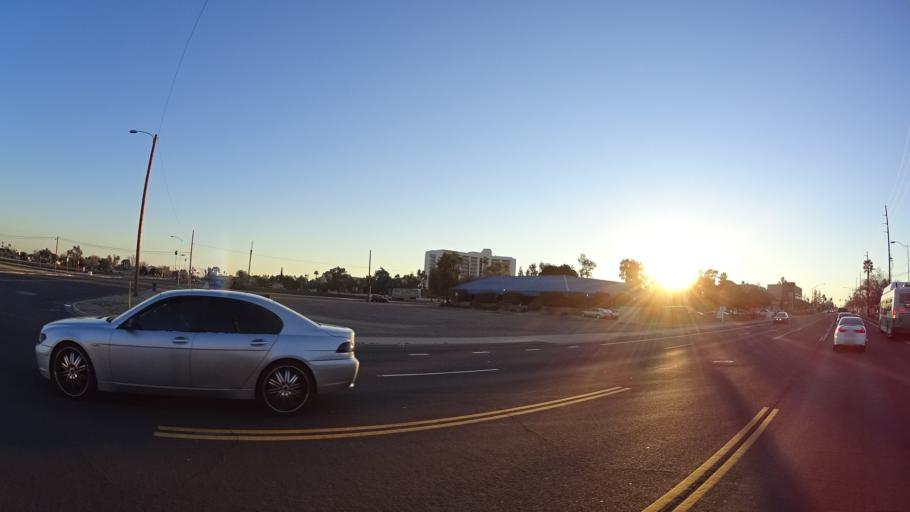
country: US
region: Arizona
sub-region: Maricopa County
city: Mesa
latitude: 33.4224
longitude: -111.8263
